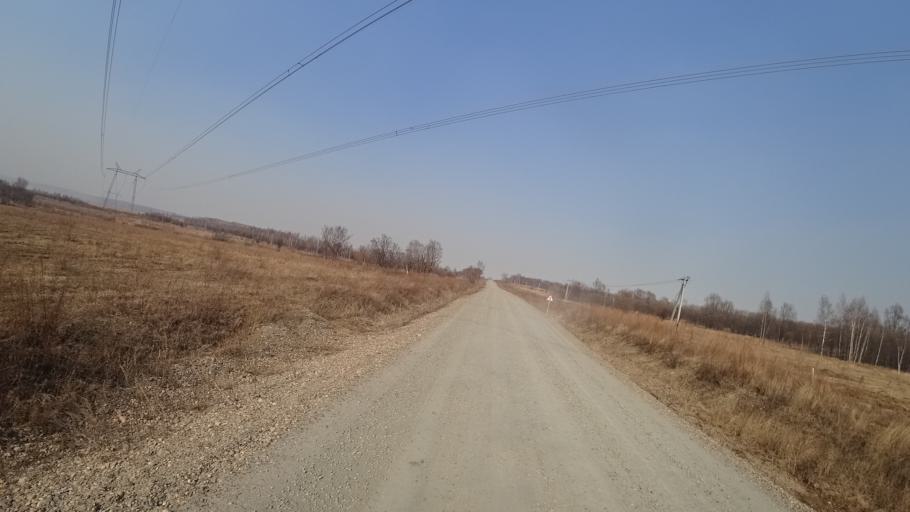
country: RU
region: Amur
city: Novobureyskiy
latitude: 49.8150
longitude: 129.9748
